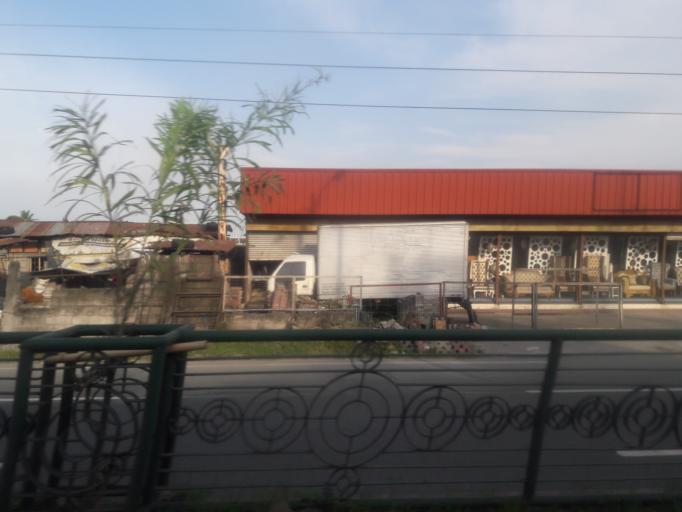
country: PH
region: Calabarzon
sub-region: Province of Cavite
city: Imus
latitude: 14.3971
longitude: 120.9400
